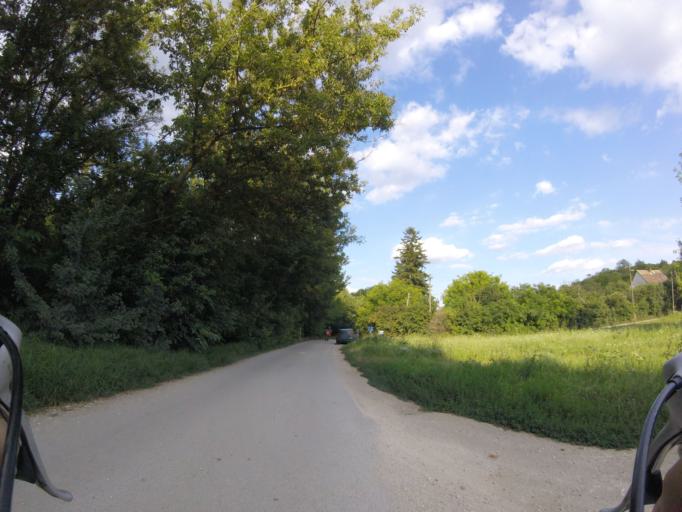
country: HU
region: Pest
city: Budaors
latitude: 47.4401
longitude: 18.9523
